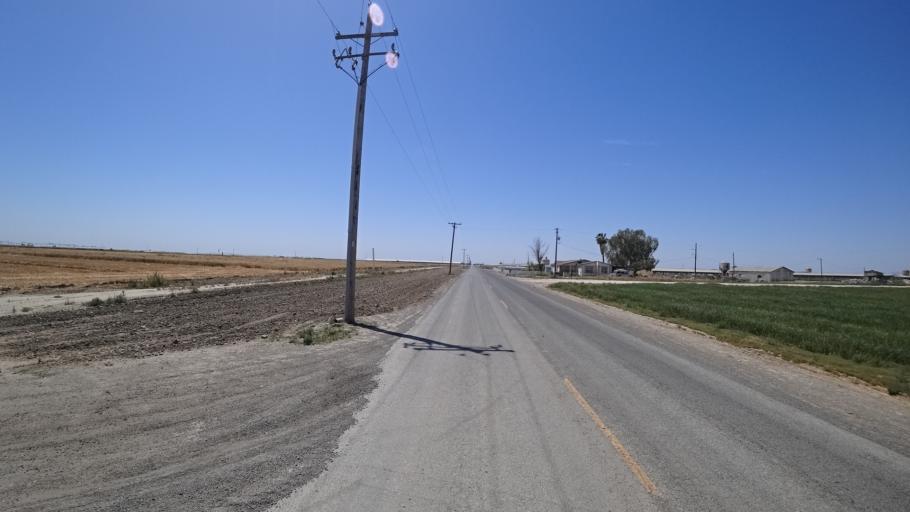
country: US
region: California
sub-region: Kings County
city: Home Garden
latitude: 36.2008
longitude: -119.6906
